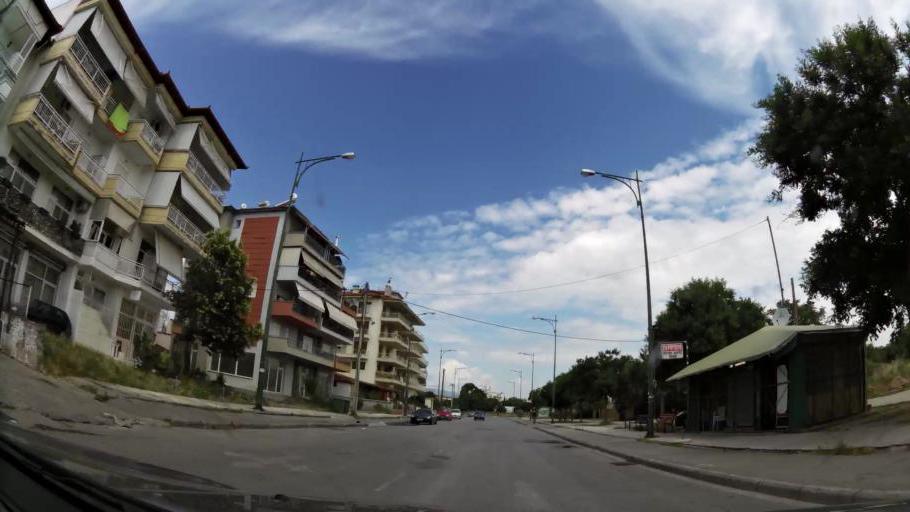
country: GR
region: Central Macedonia
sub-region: Nomos Pierias
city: Katerini
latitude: 40.2761
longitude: 22.5104
